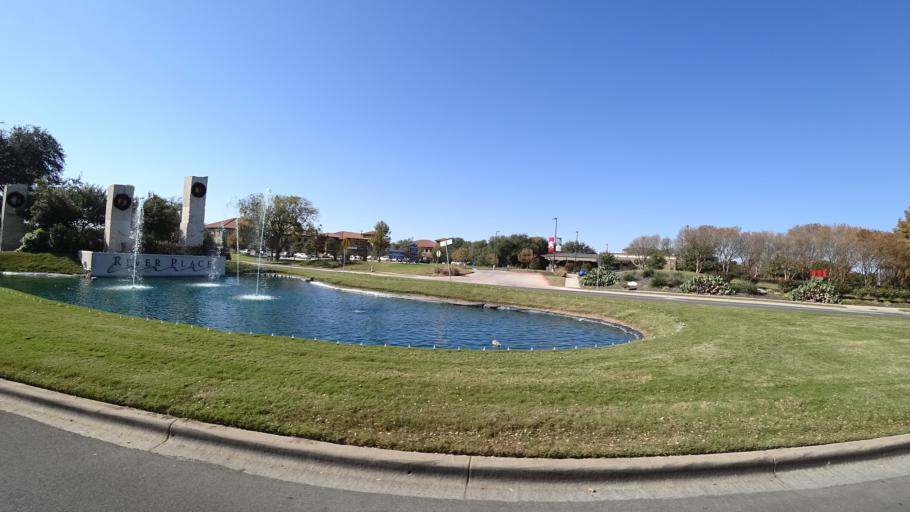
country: US
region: Texas
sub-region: Williamson County
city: Anderson Mill
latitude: 30.3938
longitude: -97.8459
